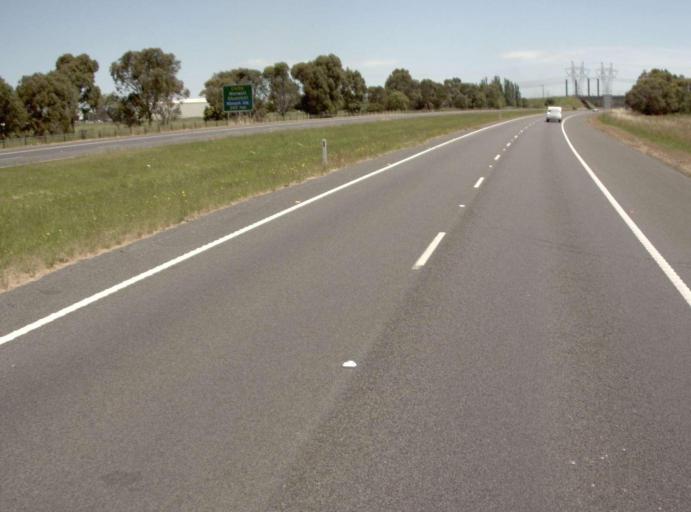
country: AU
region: Victoria
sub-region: Latrobe
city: Morwell
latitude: -38.2431
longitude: 146.4425
